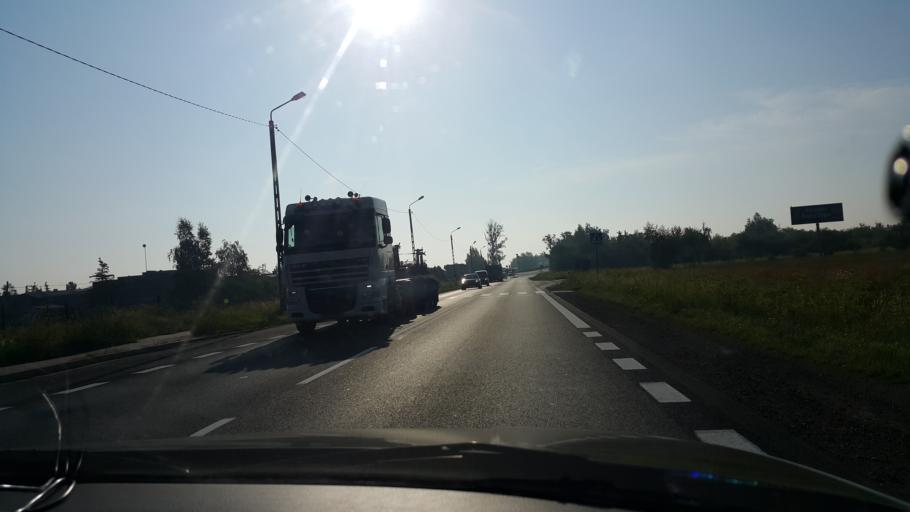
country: PL
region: Masovian Voivodeship
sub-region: Radom
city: Radom
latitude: 51.4134
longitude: 21.2302
